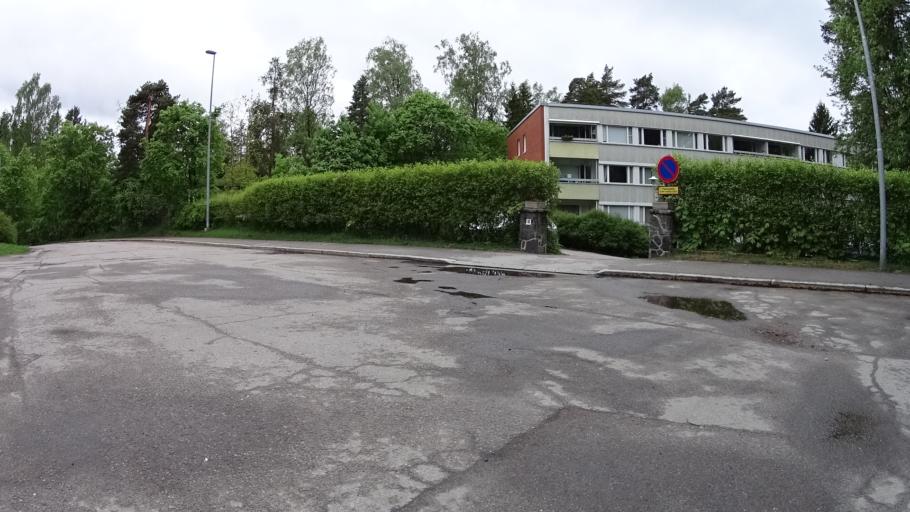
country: FI
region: Uusimaa
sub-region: Helsinki
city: Kauniainen
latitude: 60.2320
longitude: 24.7385
